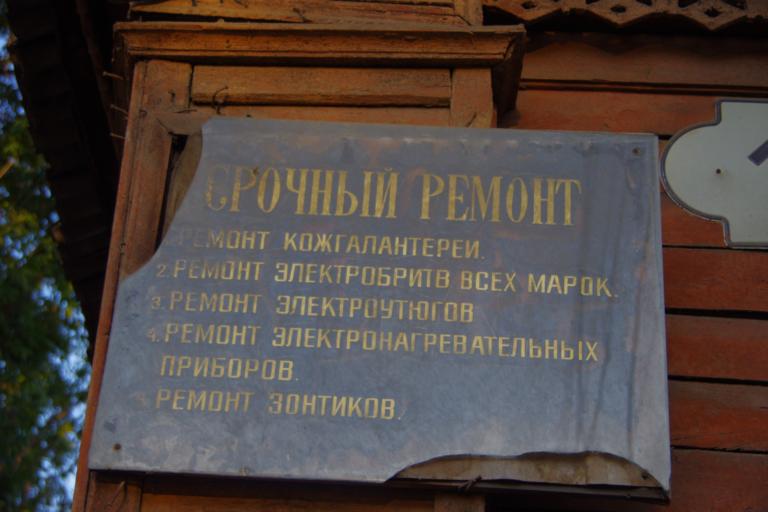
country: RU
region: Samara
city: Samara
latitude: 53.1923
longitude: 50.1051
